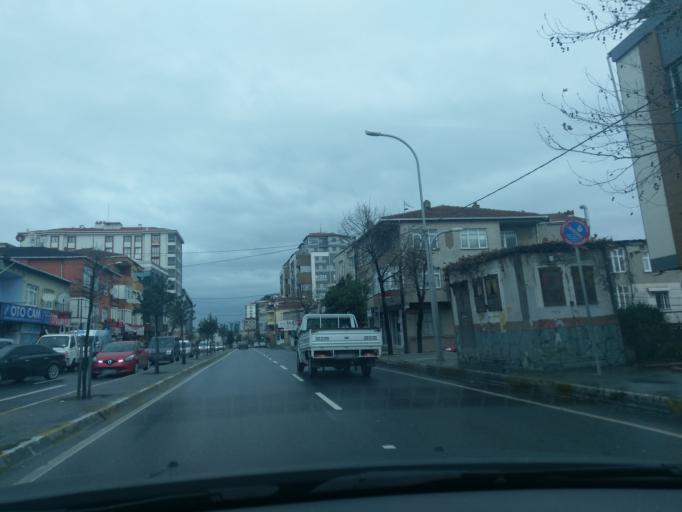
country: TR
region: Istanbul
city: Mahmutbey
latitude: 41.0484
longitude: 28.8304
